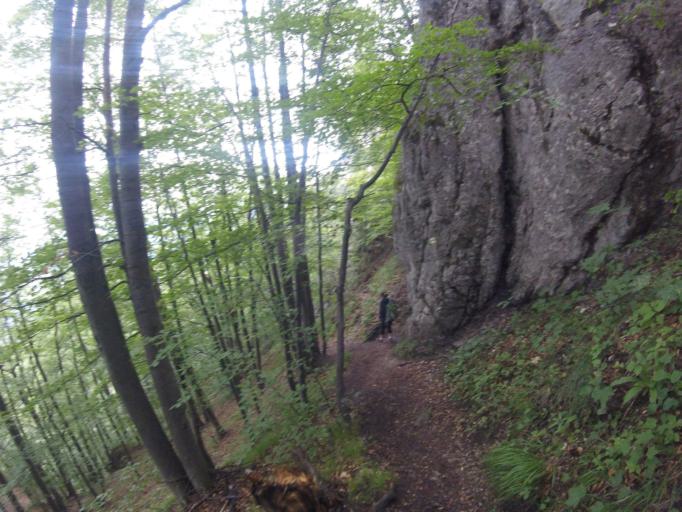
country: SK
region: Zilinsky
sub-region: Okres Zilina
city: Terchova
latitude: 49.2349
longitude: 19.0094
